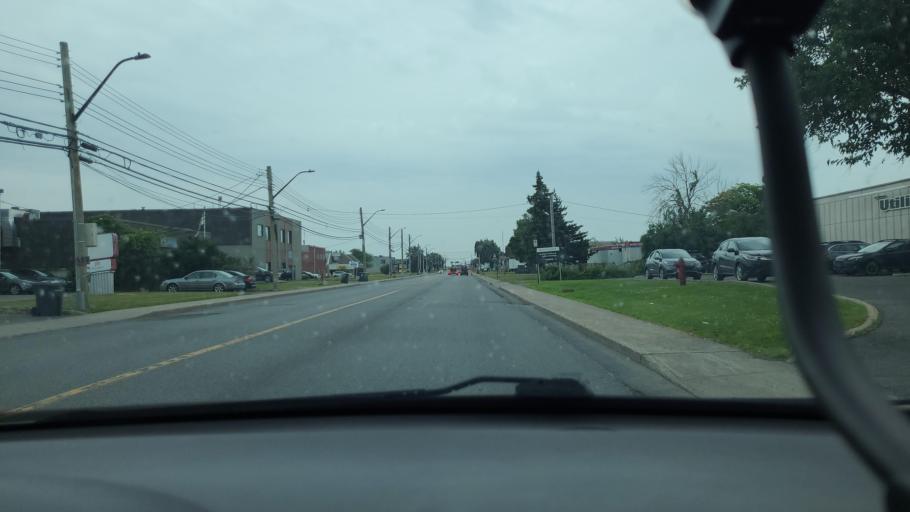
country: CA
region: Quebec
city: Hampstead
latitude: 45.4825
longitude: -73.7120
